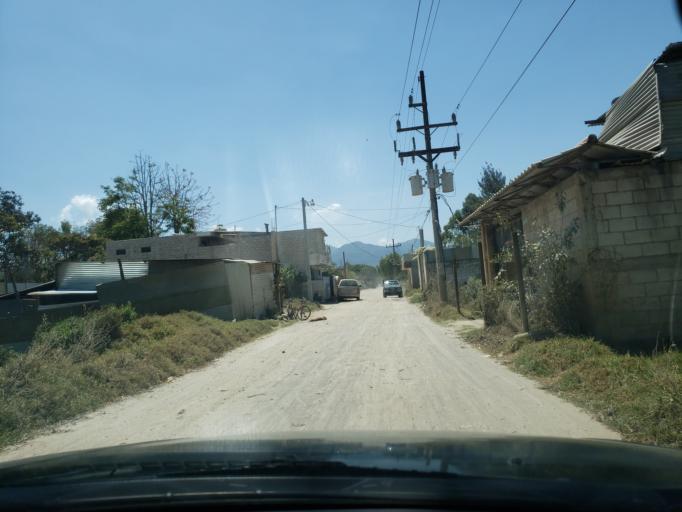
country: GT
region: Chimaltenango
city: El Tejar
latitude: 14.6482
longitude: -90.8033
